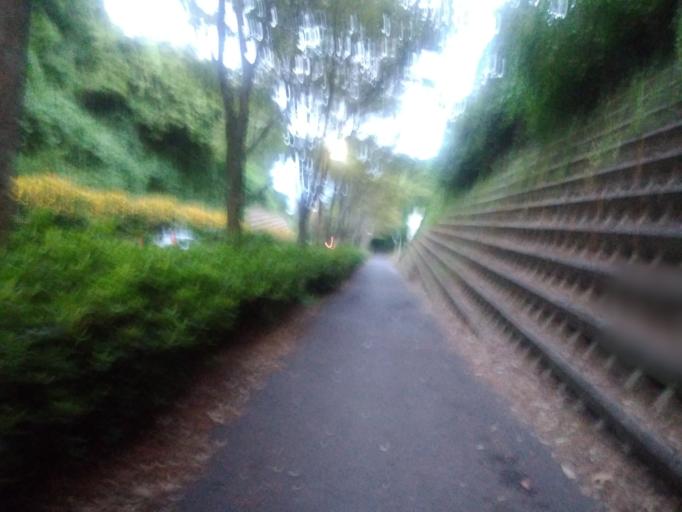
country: JP
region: Hiroshima
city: Onomichi
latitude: 34.4326
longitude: 133.1760
